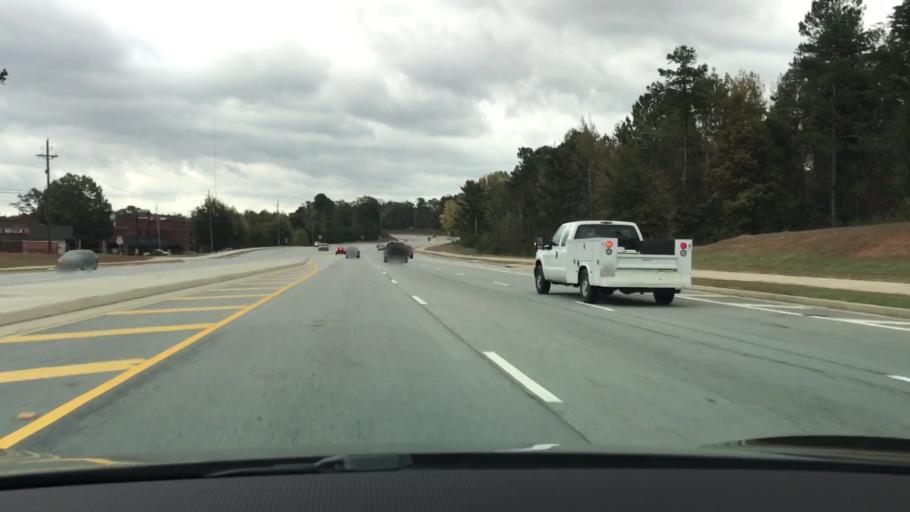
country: US
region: Georgia
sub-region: Hall County
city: Flowery Branch
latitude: 34.1389
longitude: -83.9487
